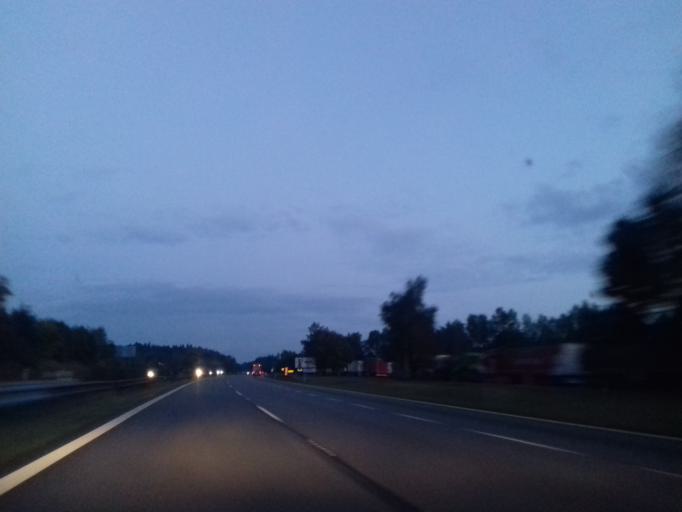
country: CZ
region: Vysocina
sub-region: Okres Pelhrimov
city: Zeliv
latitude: 49.5683
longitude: 15.2823
